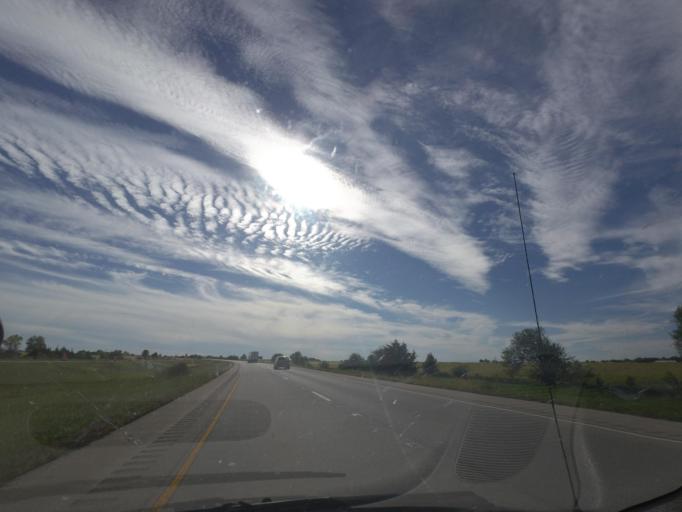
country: US
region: Illinois
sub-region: Piatt County
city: Cerro Gordo
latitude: 39.9751
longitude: -88.8049
